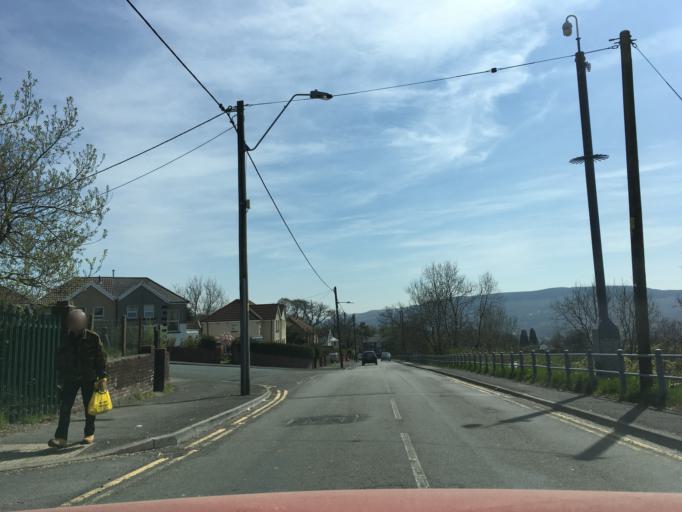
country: GB
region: Wales
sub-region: Merthyr Tydfil County Borough
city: Merthyr Tydfil
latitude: 51.7632
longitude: -3.3724
